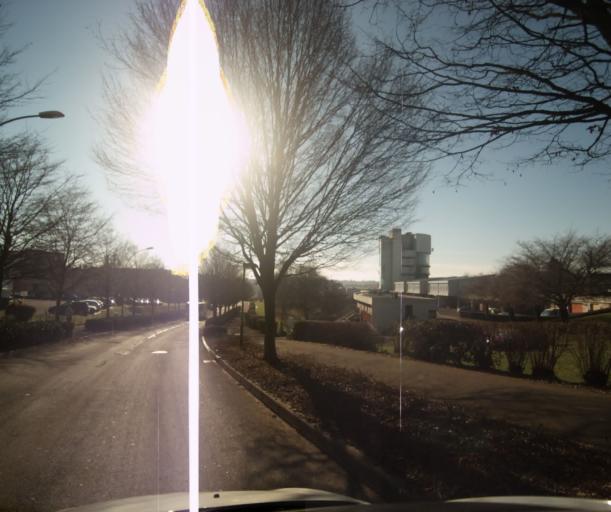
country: FR
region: Franche-Comte
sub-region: Departement du Doubs
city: Besancon
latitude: 47.2544
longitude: 6.0025
